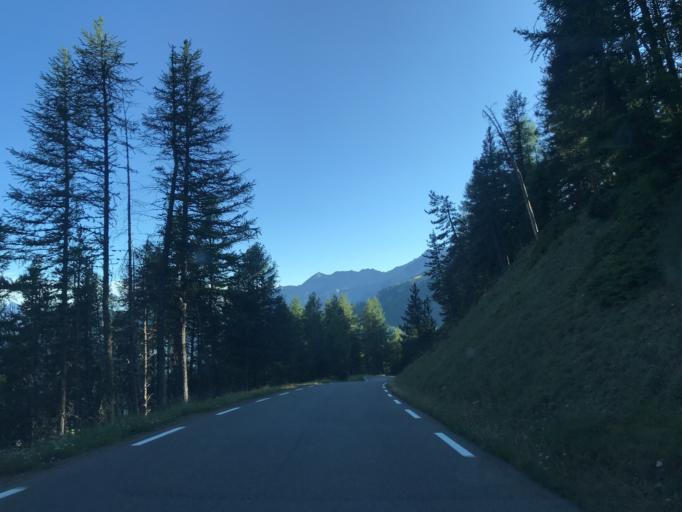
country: FR
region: Provence-Alpes-Cote d'Azur
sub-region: Departement des Hautes-Alpes
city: Villar-Saint-Pancrace
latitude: 44.8037
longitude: 6.7343
